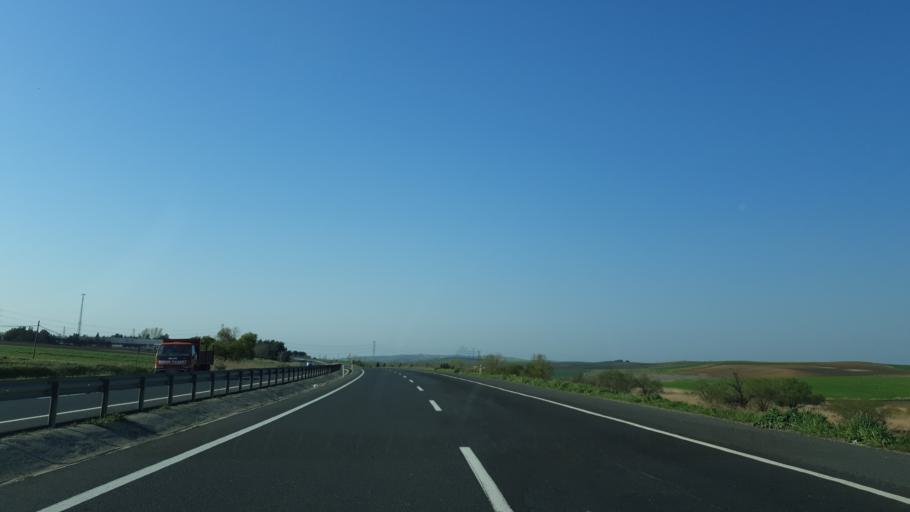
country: TR
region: Tekirdag
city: Corlu
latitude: 41.1175
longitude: 27.7496
